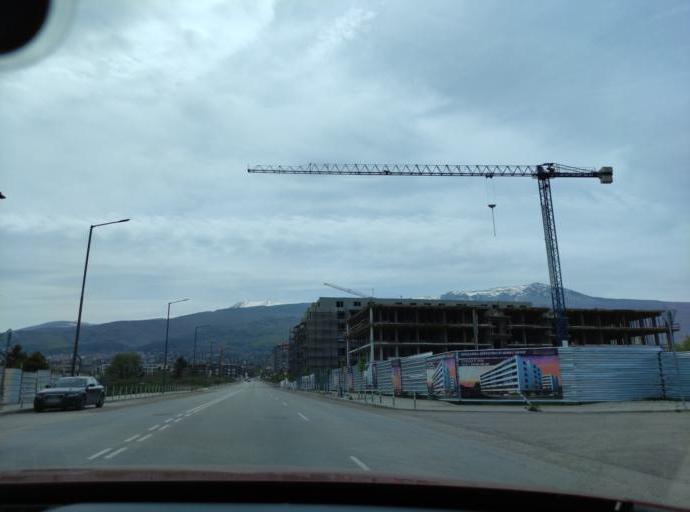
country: BG
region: Sofia-Capital
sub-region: Stolichna Obshtina
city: Sofia
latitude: 42.6412
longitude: 23.3443
